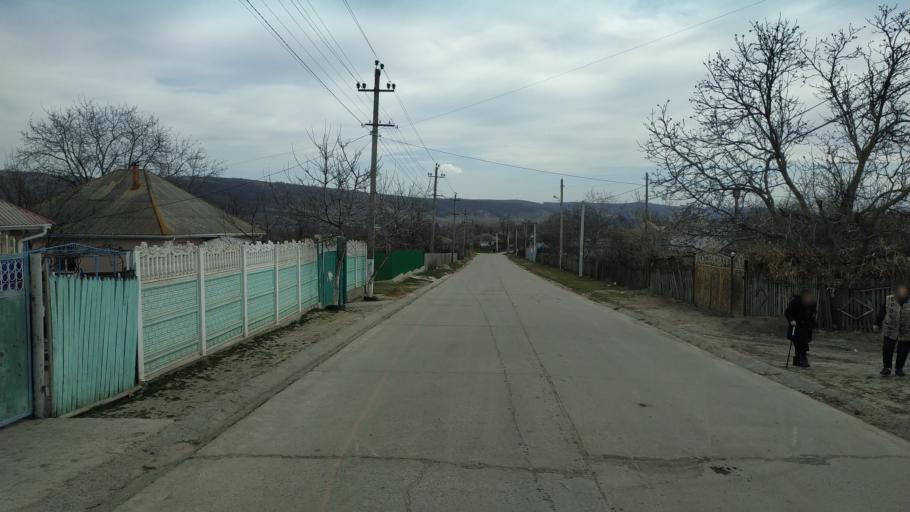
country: MD
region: Nisporeni
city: Nisporeni
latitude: 46.9277
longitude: 28.2607
